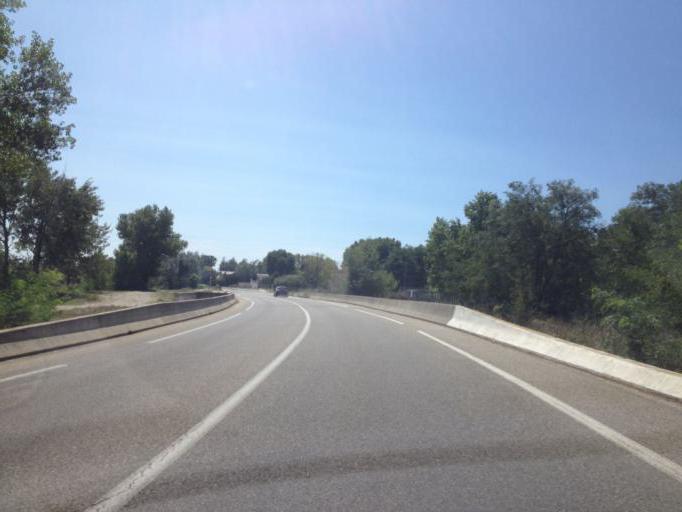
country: FR
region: Languedoc-Roussillon
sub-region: Departement du Gard
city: Roquemaure
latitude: 44.0543
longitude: 4.7830
